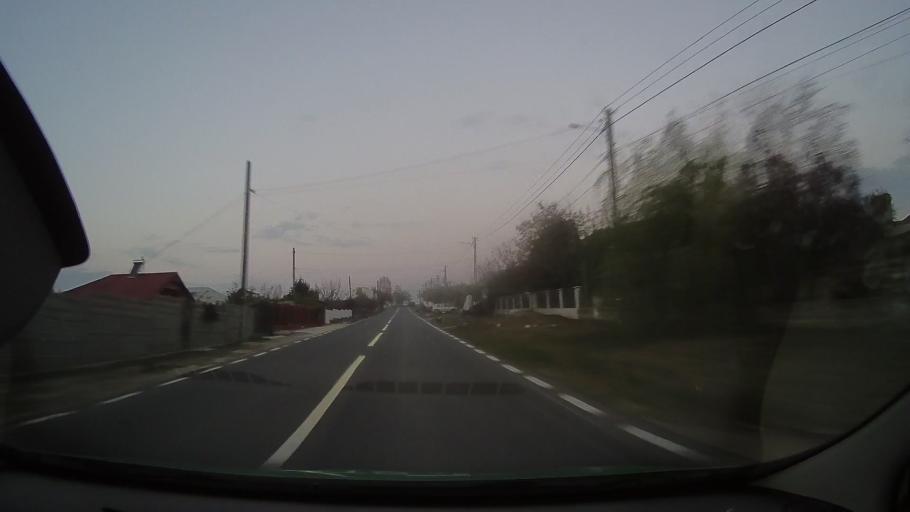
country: RO
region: Constanta
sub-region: Comuna Baneasa
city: Baneasa
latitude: 44.0658
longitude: 27.7101
